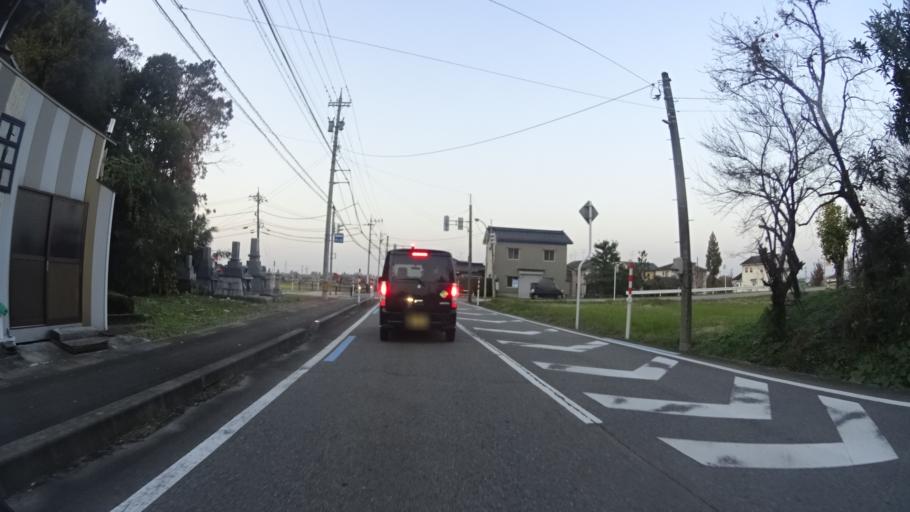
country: JP
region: Toyama
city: Kamiichi
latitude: 36.7192
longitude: 137.3690
